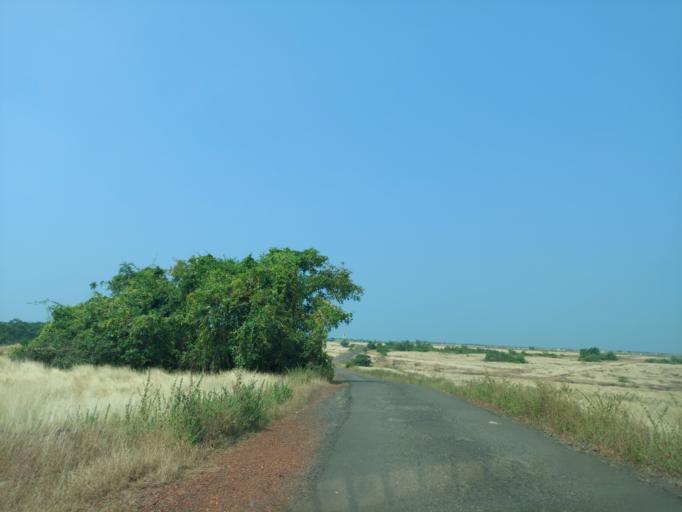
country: IN
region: Maharashtra
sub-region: Sindhudurg
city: Malvan
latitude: 15.9961
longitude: 73.5198
